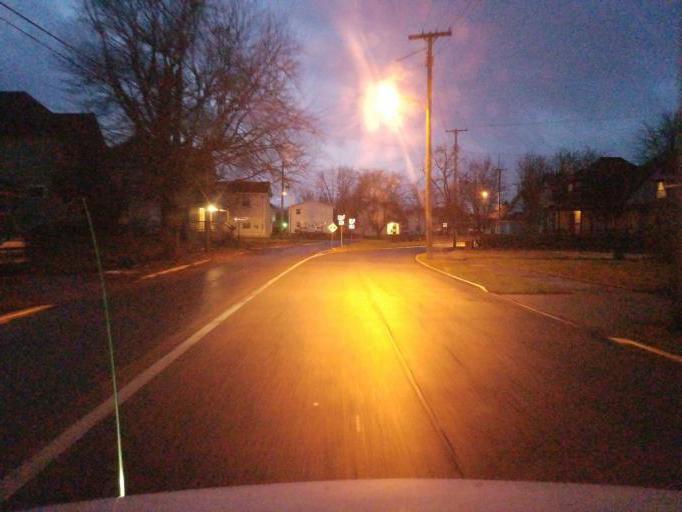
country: US
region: Ohio
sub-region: Marion County
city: Marion
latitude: 40.5799
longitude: -83.1298
